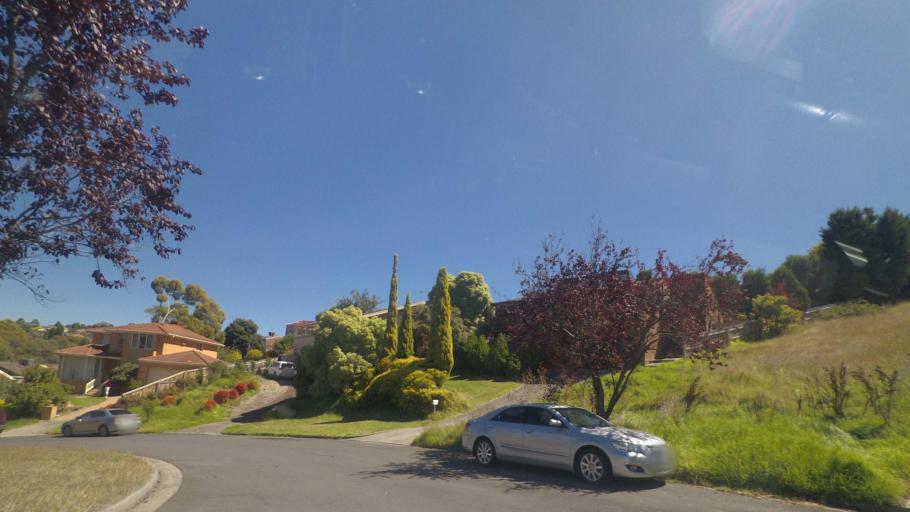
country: AU
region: Victoria
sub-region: Manningham
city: Donvale
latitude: -37.7672
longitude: 145.1770
